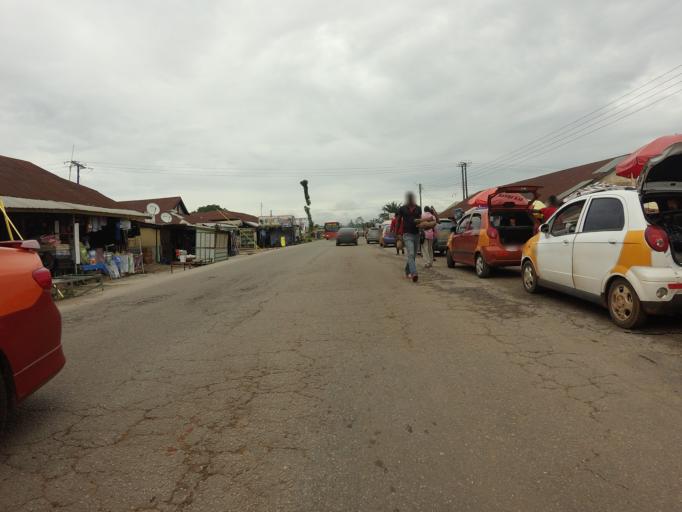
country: GH
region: Eastern
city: Begoro
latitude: 6.3821
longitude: -0.5502
